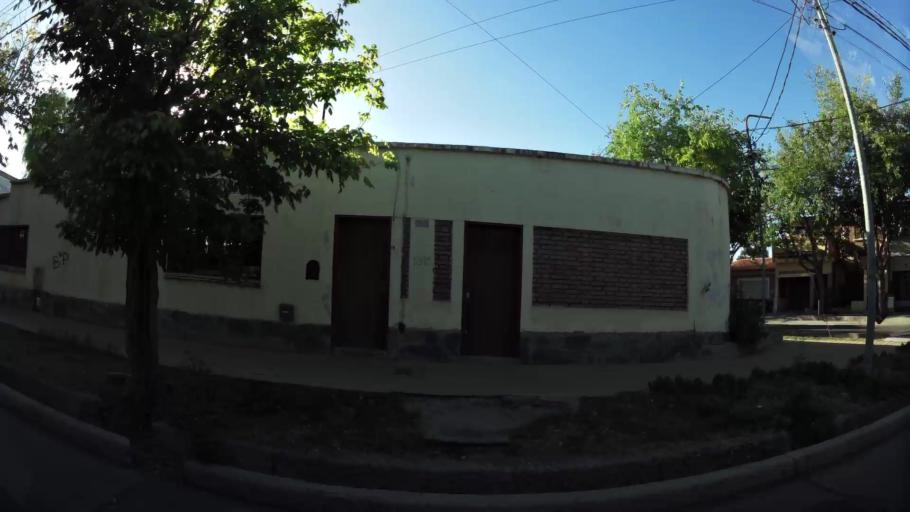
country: AR
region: Mendoza
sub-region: Departamento de Godoy Cruz
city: Godoy Cruz
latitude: -32.9404
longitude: -68.8453
